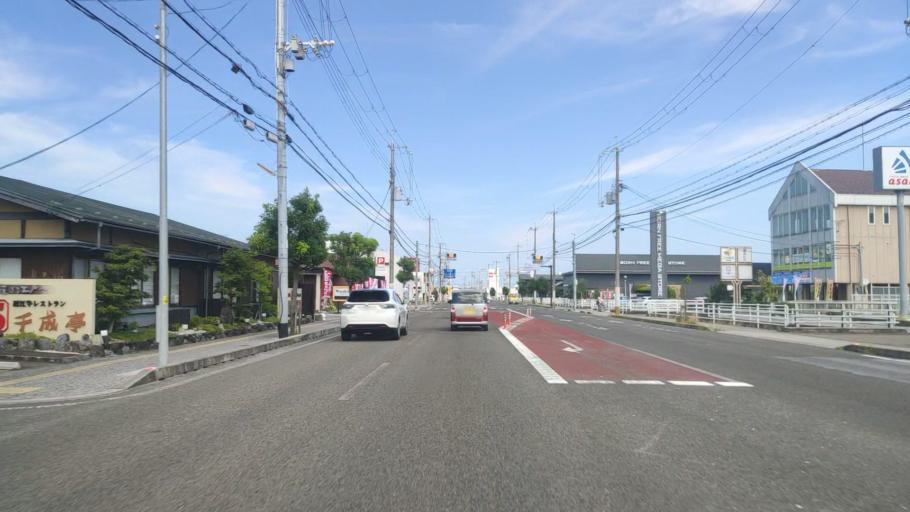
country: JP
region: Shiga Prefecture
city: Hikone
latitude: 35.2546
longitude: 136.2390
